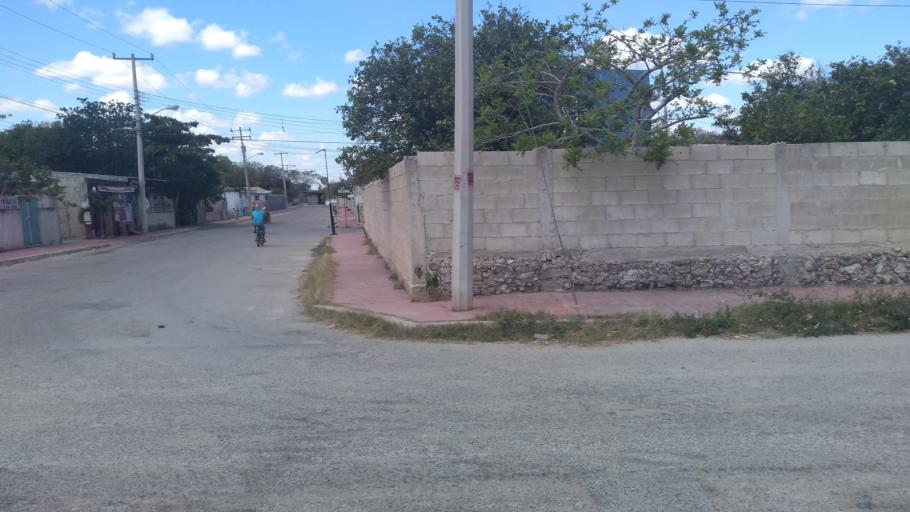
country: MX
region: Yucatan
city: Itzincab Palomeque
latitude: 20.9255
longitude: -89.6695
